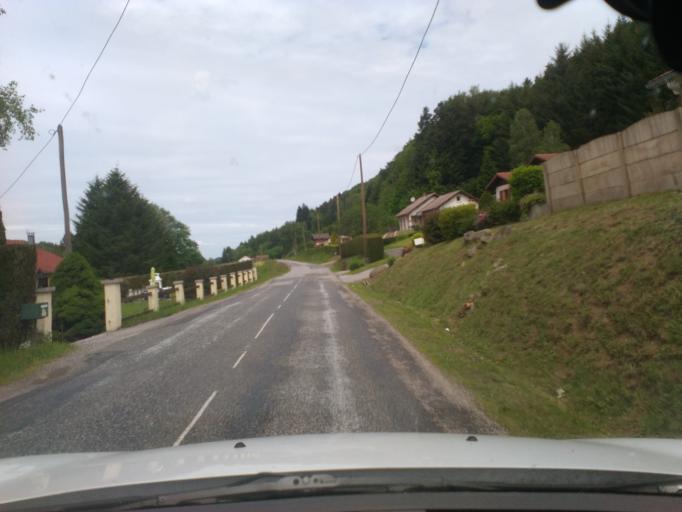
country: FR
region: Lorraine
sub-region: Departement des Vosges
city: Le Tholy
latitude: 48.1232
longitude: 6.7262
